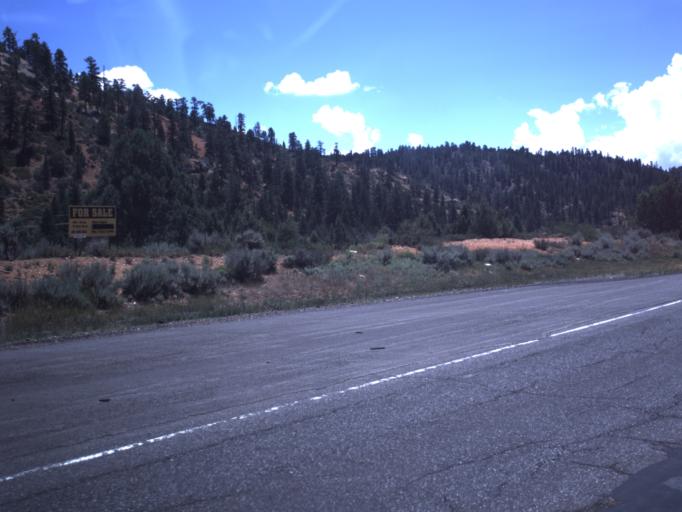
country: US
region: Utah
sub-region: Kane County
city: Kanab
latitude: 37.4013
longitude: -112.5566
